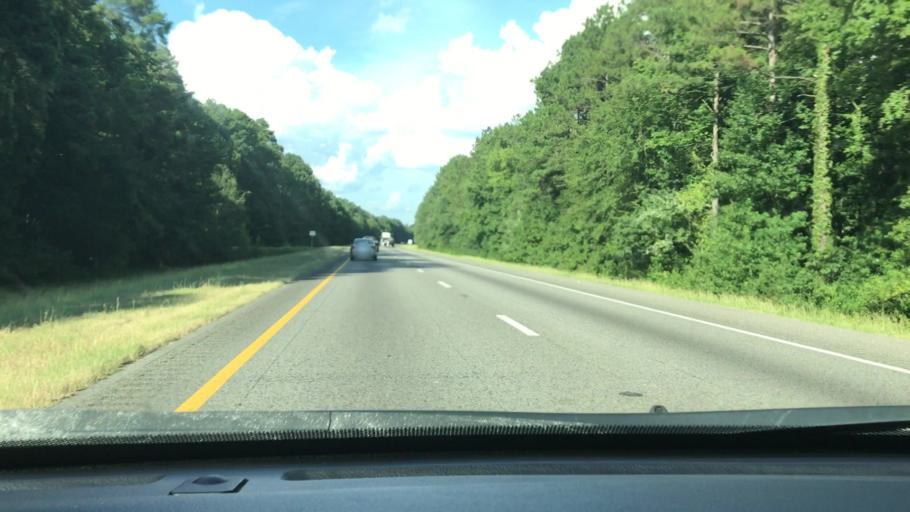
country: US
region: South Carolina
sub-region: Florence County
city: Florence
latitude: 34.3068
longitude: -79.6204
